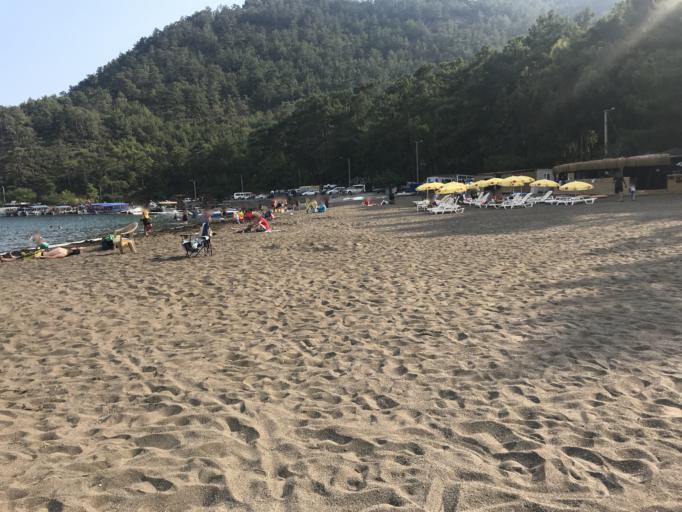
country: TR
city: Dalyan
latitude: 36.8303
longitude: 28.5490
